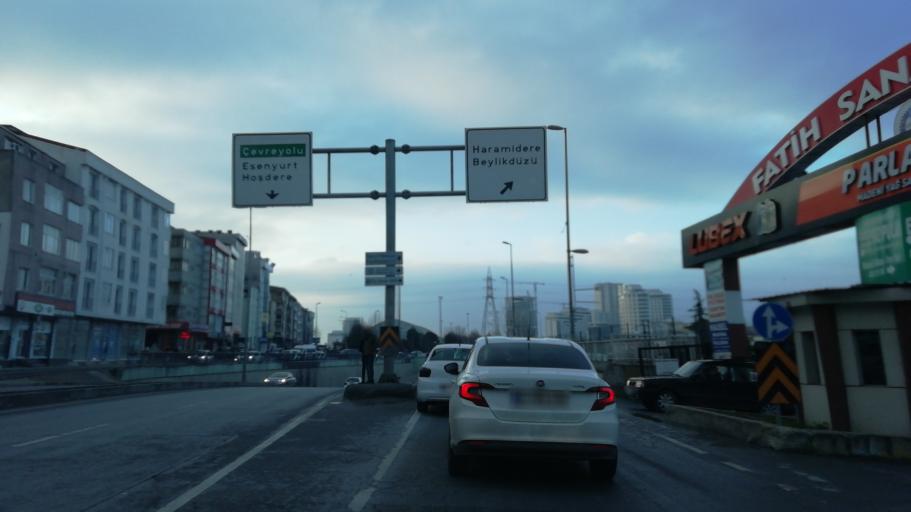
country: TR
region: Istanbul
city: Esenyurt
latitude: 41.0140
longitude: 28.6936
